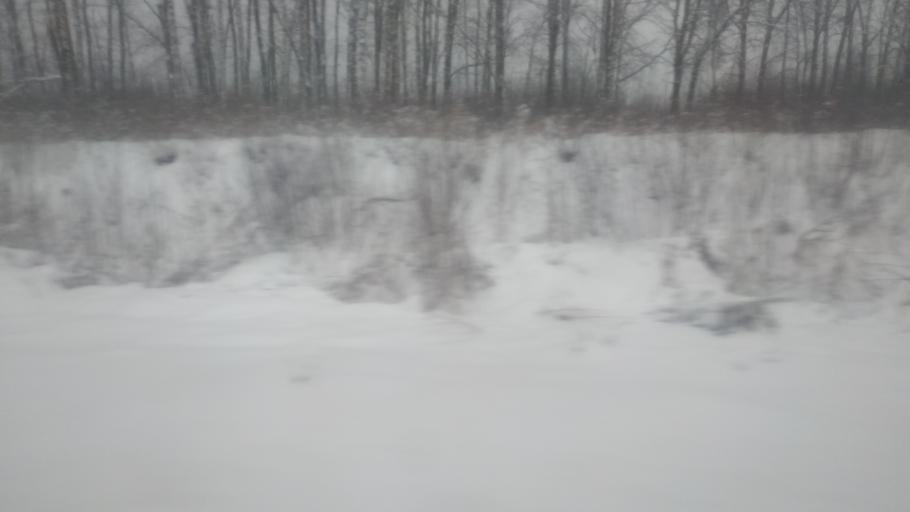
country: RU
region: Bashkortostan
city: Amzya
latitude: 56.2399
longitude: 54.5391
